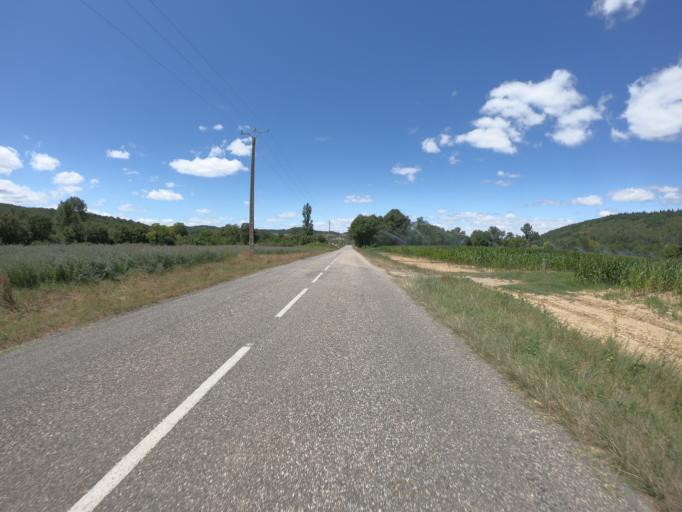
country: FR
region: Midi-Pyrenees
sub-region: Departement de l'Ariege
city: Verniolle
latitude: 43.0534
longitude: 1.7530
